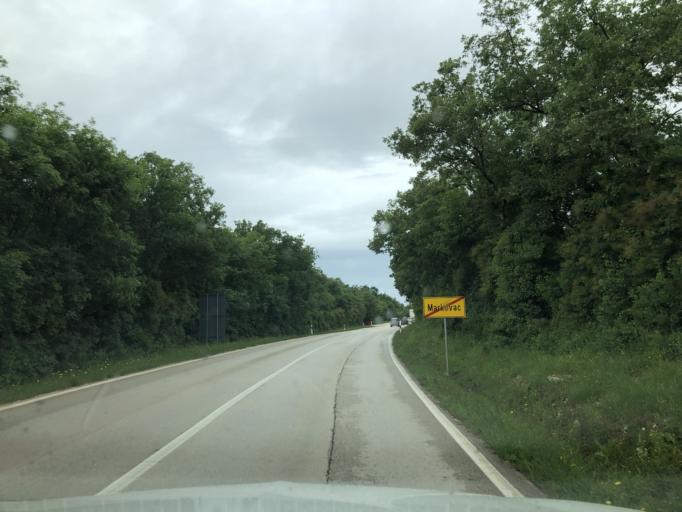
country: SI
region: Piran-Pirano
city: Seca
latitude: 45.4543
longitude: 13.6150
